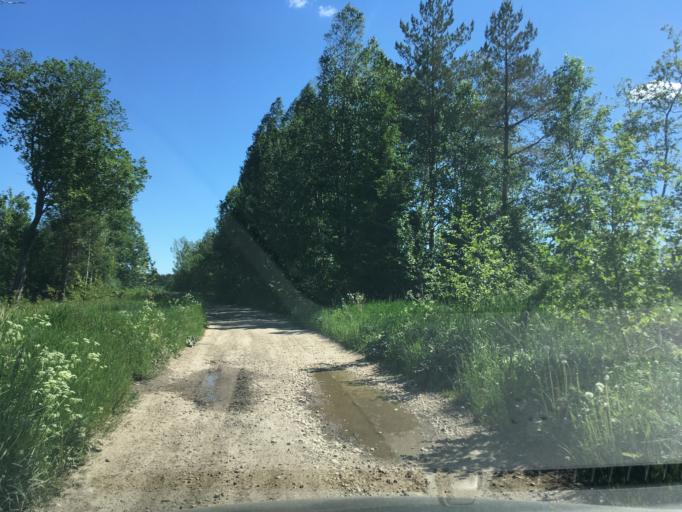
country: EE
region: Harju
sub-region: Raasiku vald
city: Raasiku
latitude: 59.1542
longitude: 25.1466
